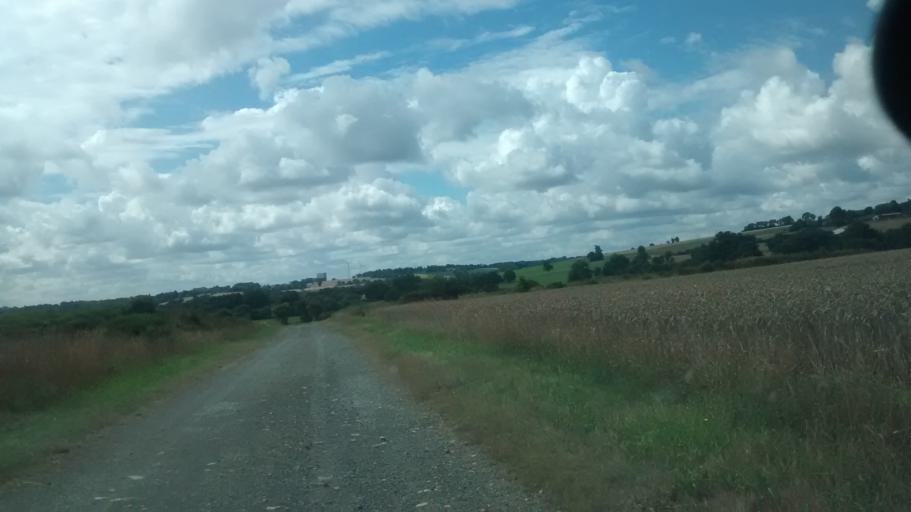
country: FR
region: Brittany
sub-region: Departement d'Ille-et-Vilaine
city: La Dominelais
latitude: 47.7780
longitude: -1.7262
